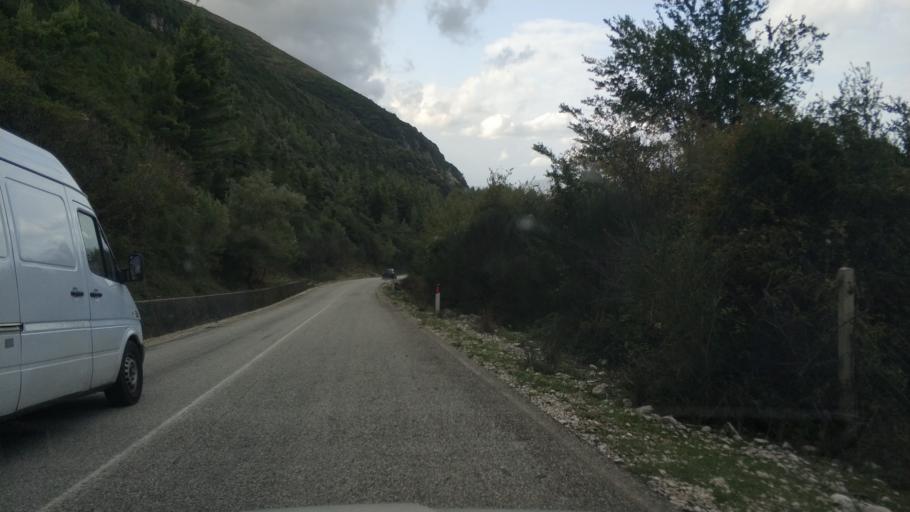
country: AL
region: Vlore
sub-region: Rrethi i Vlores
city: Orikum
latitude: 40.2553
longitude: 19.5318
